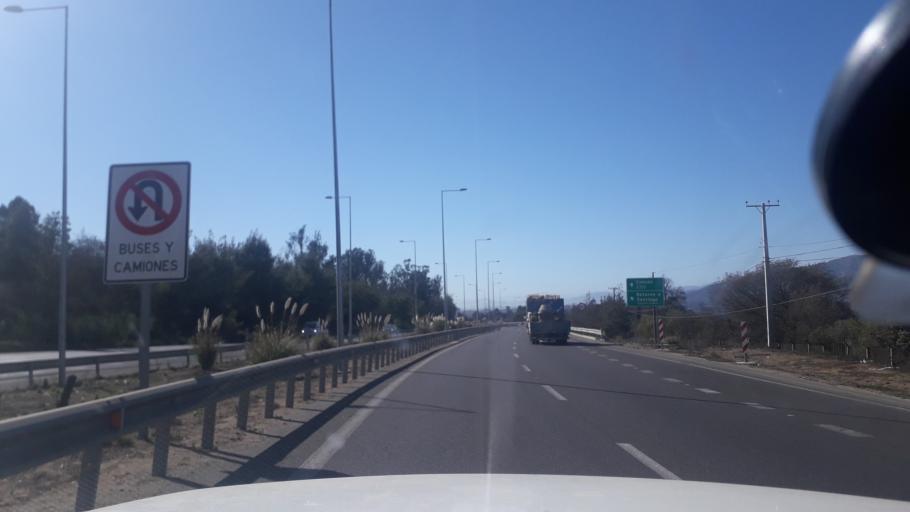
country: CL
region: Valparaiso
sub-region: Provincia de Valparaiso
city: Vina del Mar
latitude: -32.9572
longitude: -71.5103
